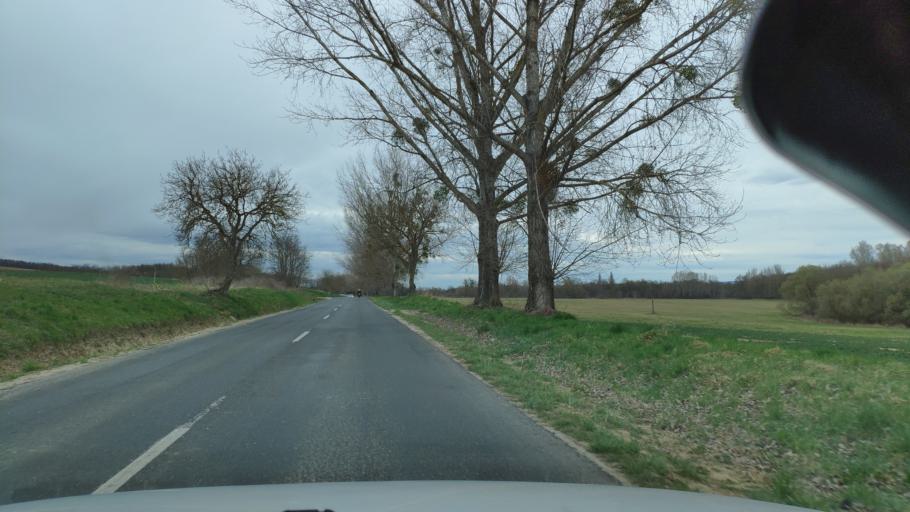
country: HU
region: Zala
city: Sarmellek
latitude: 46.6613
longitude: 17.1138
